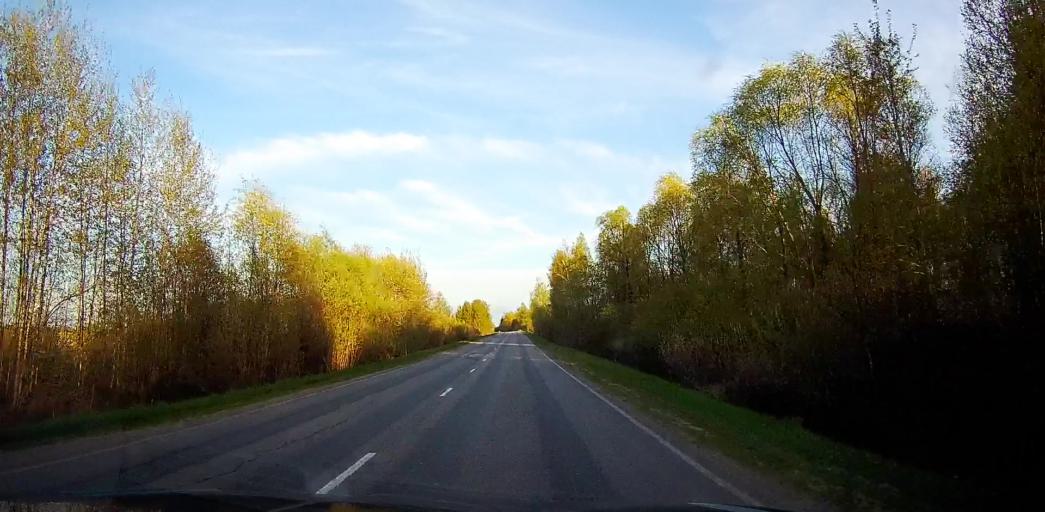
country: RU
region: Moskovskaya
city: Bronnitsy
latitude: 55.2768
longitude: 38.2229
